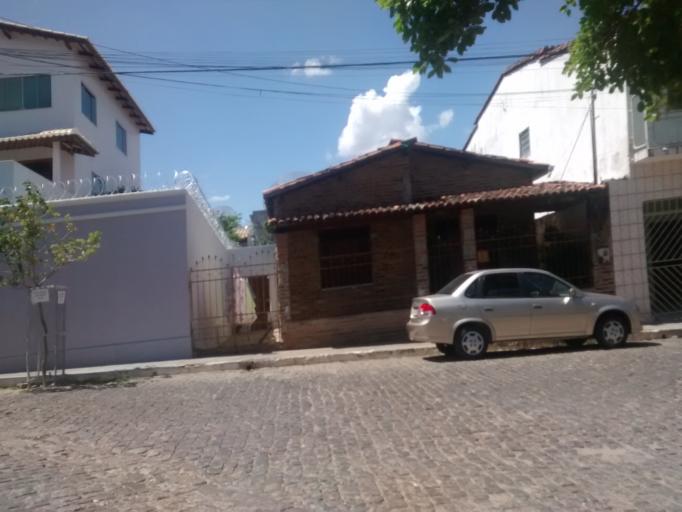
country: BR
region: Bahia
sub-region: Brumado
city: Brumado
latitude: -14.2075
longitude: -41.6734
